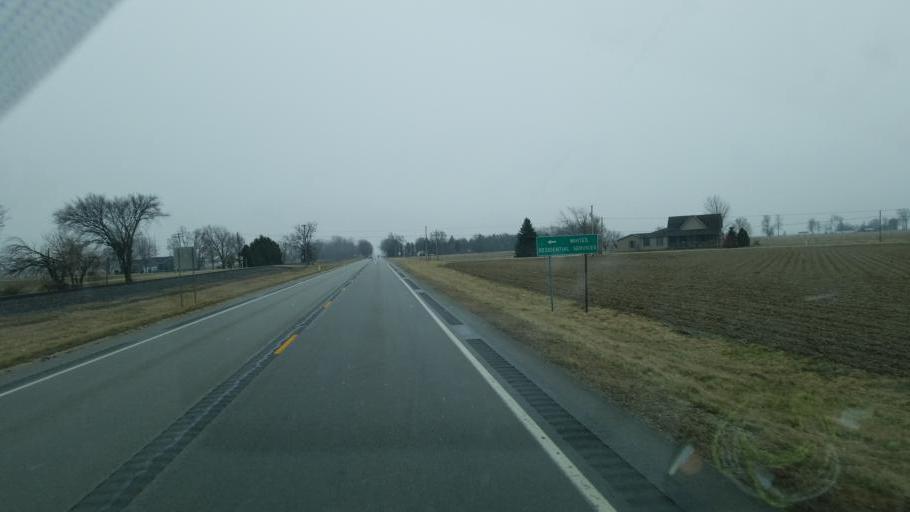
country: US
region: Indiana
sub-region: Wabash County
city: Wabash
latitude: 40.7547
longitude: -85.8078
